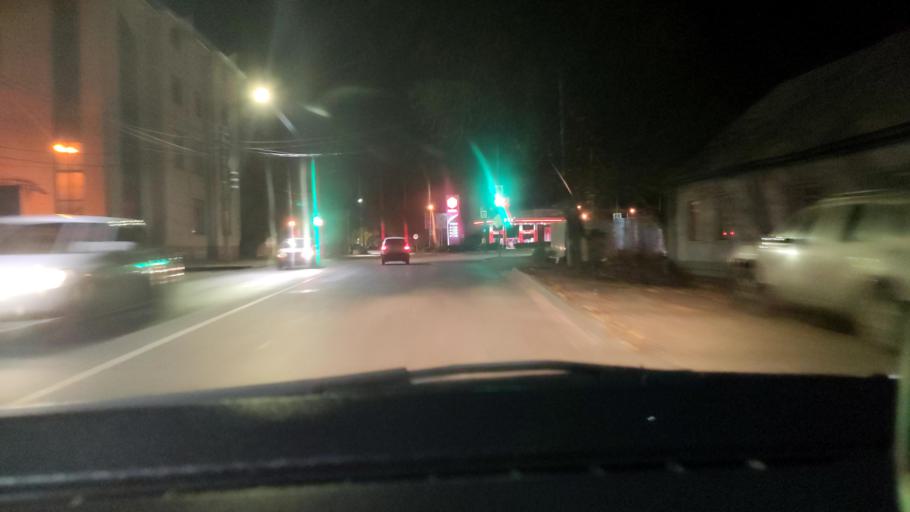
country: RU
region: Voronezj
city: Voronezh
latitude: 51.6824
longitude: 39.2063
